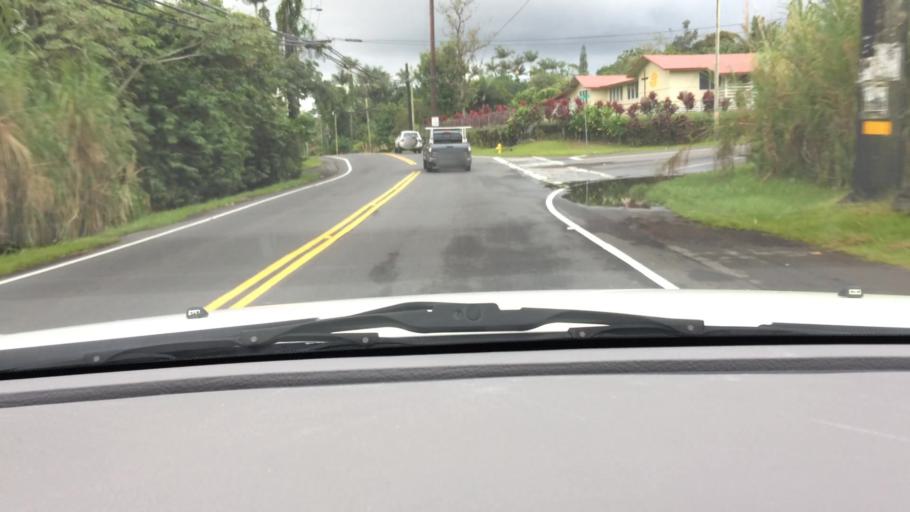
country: US
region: Hawaii
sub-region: Hawaii County
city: Hawaiian Paradise Park
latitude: 19.4996
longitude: -154.9540
